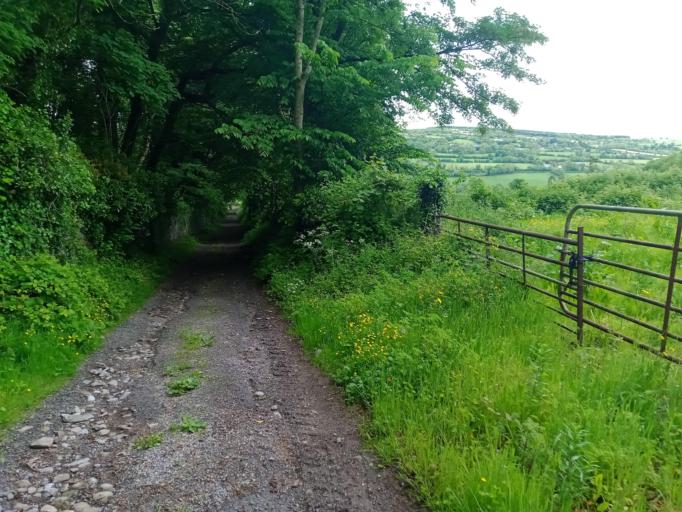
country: IE
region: Leinster
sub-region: Kilkenny
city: Thomastown
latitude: 52.4778
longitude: -7.0588
